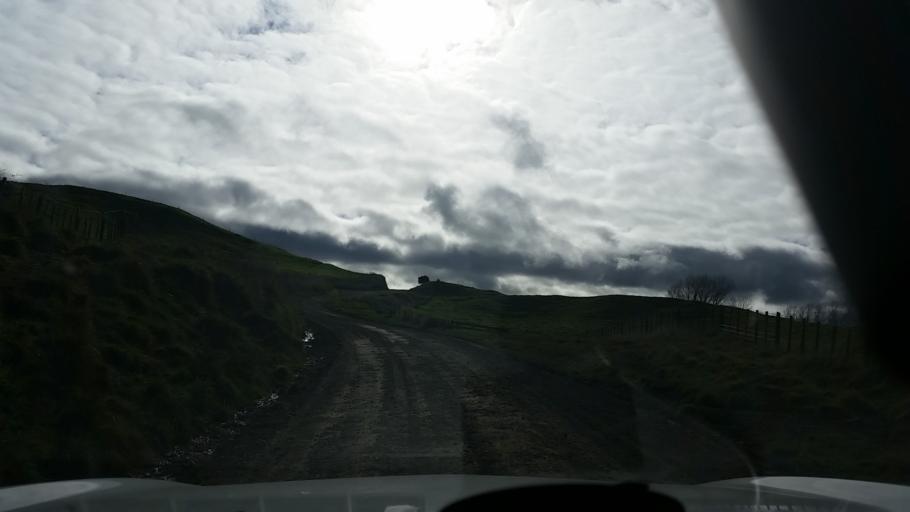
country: NZ
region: Hawke's Bay
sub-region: Napier City
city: Napier
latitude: -39.1168
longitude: 176.8956
